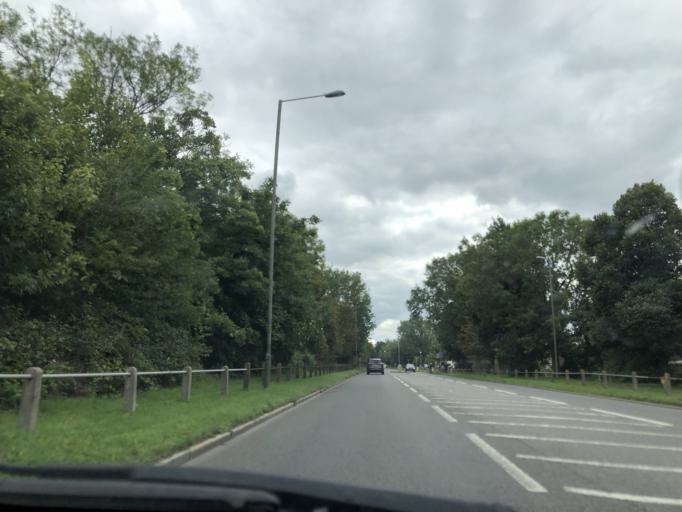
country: GB
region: England
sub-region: Greater London
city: Orpington
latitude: 51.3640
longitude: 0.1123
